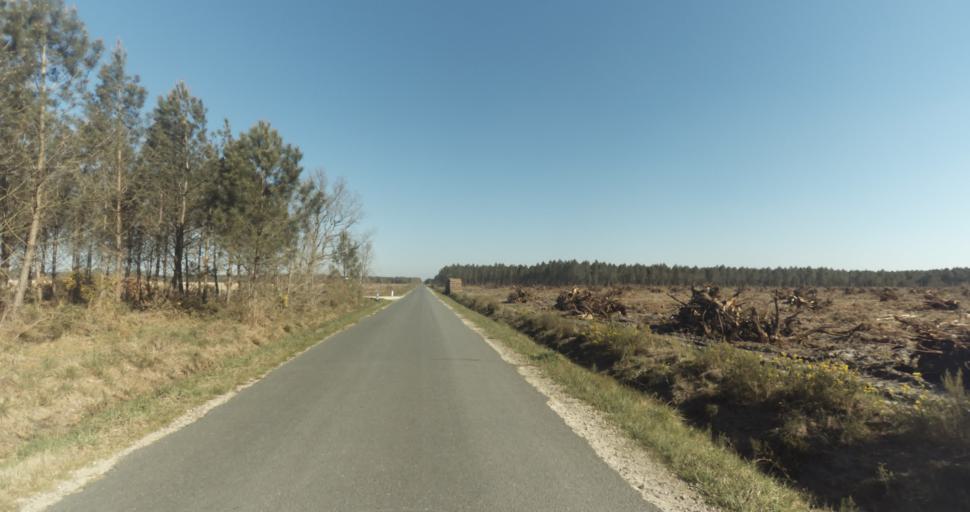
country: FR
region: Aquitaine
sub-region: Departement de la Gironde
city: Marcheprime
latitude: 44.7765
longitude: -0.8591
